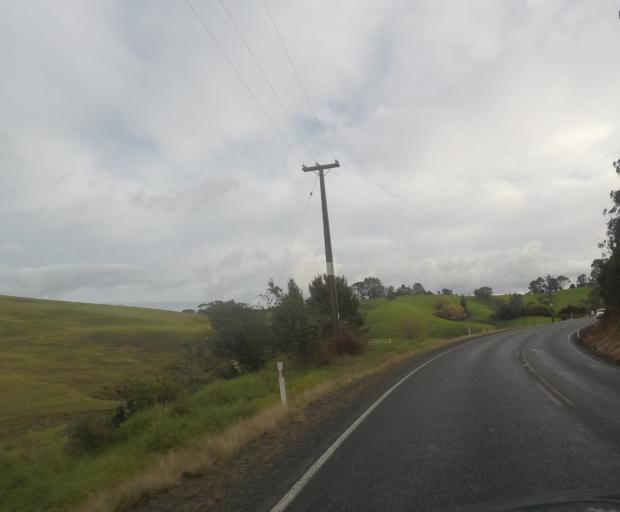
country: NZ
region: Auckland
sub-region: Auckland
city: Wellsford
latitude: -36.1758
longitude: 174.5822
